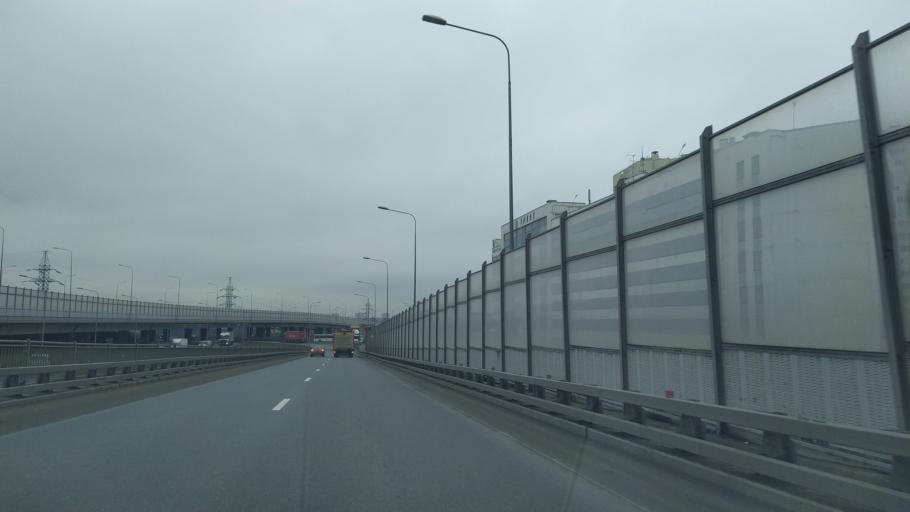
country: RU
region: St.-Petersburg
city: Kupchino
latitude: 59.8312
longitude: 30.3138
